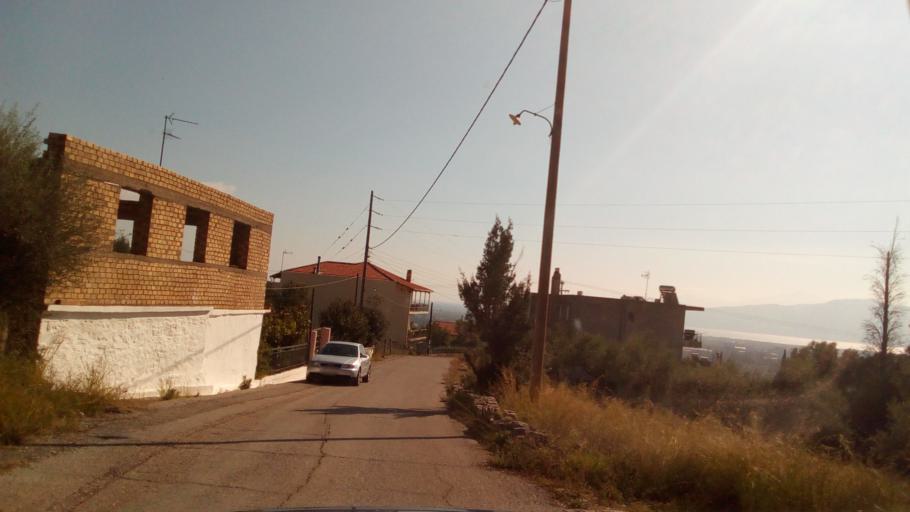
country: GR
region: West Greece
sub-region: Nomos Aitolias kai Akarnanias
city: Nafpaktos
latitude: 38.4198
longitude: 21.8698
